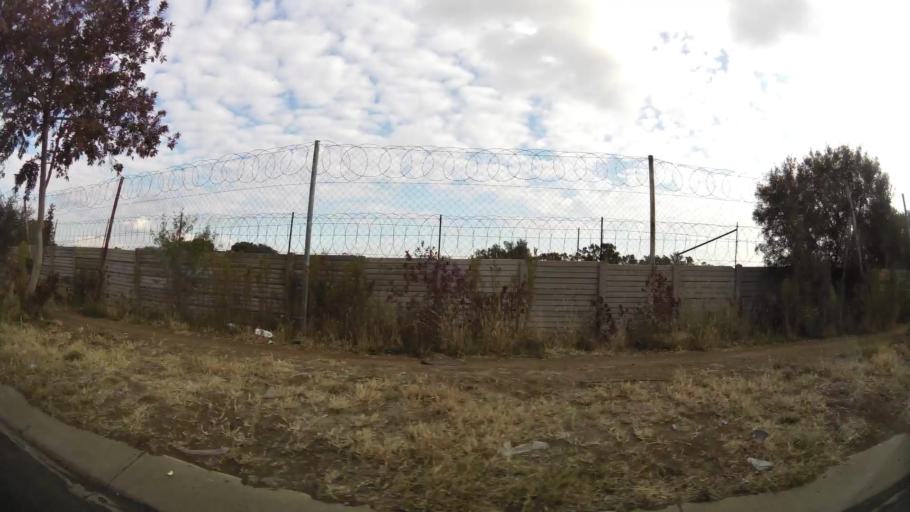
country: ZA
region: Orange Free State
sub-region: Mangaung Metropolitan Municipality
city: Bloemfontein
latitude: -29.0790
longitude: 26.1951
